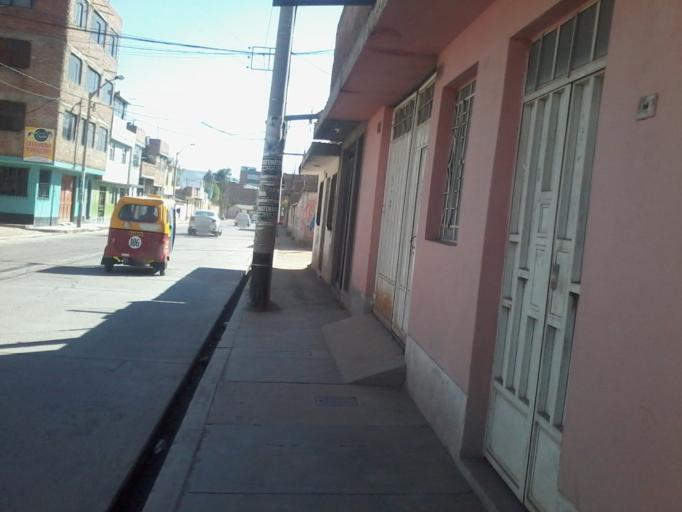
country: PE
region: Ayacucho
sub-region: Provincia de Huamanga
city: Ayacucho
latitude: -13.1656
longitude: -74.2110
